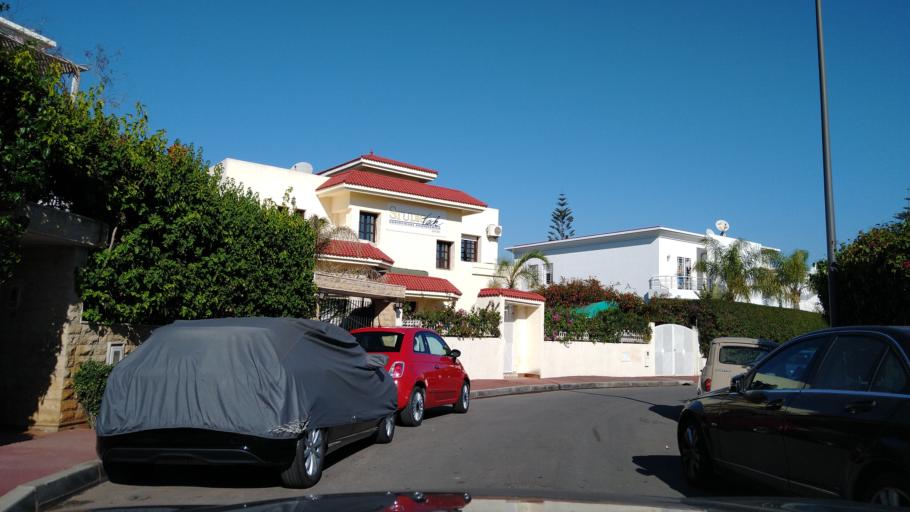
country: MA
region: Rabat-Sale-Zemmour-Zaer
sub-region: Skhirate-Temara
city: Temara
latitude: 33.9494
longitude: -6.8642
